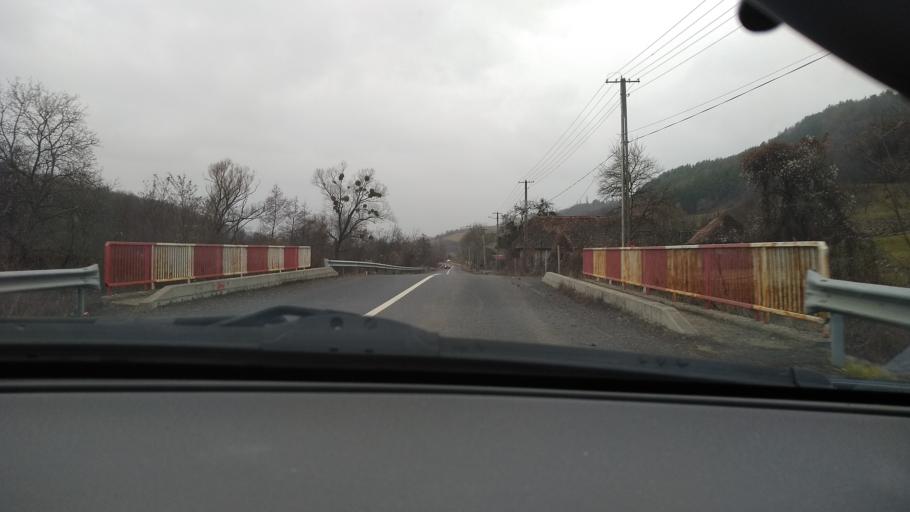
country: RO
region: Mures
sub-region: Comuna Magherani
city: Magherani
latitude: 46.5777
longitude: 24.9327
